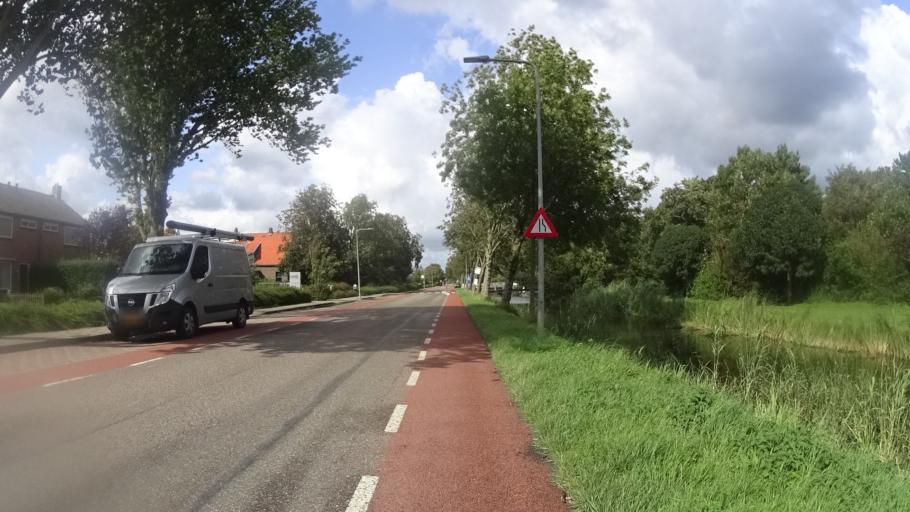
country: NL
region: North Holland
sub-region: Gemeente Schagen
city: Schagen
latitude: 52.8367
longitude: 4.8604
